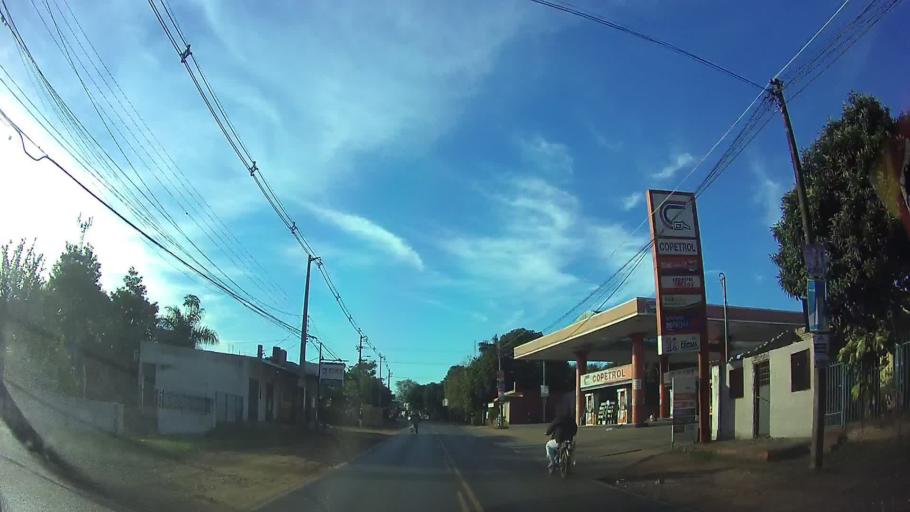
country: PY
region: Central
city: Limpio
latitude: -25.2384
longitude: -57.4745
